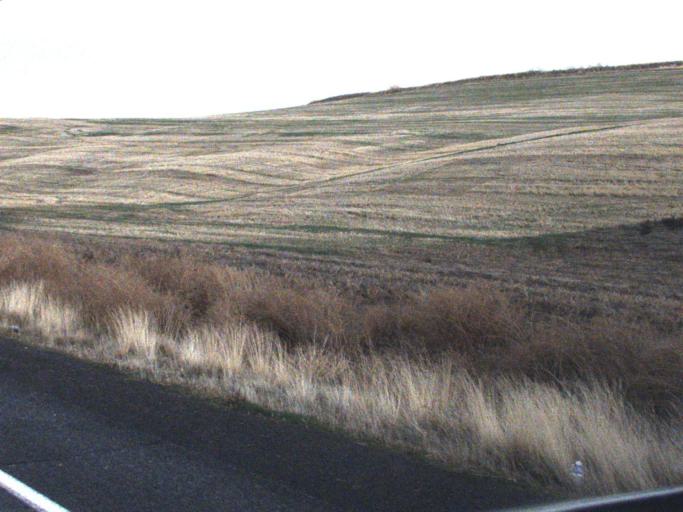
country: US
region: Washington
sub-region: Walla Walla County
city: Waitsburg
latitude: 46.1911
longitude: -118.1376
